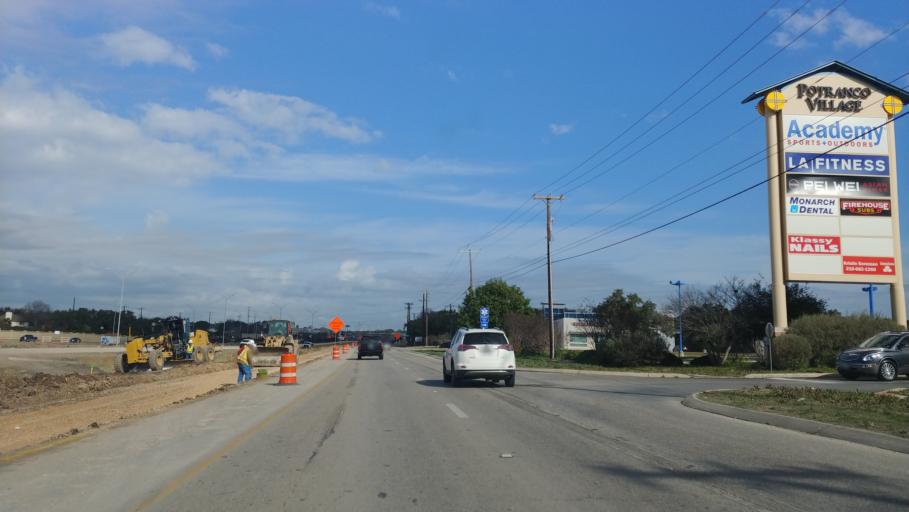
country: US
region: Texas
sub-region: Bexar County
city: Lackland Air Force Base
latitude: 29.4387
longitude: -98.7107
